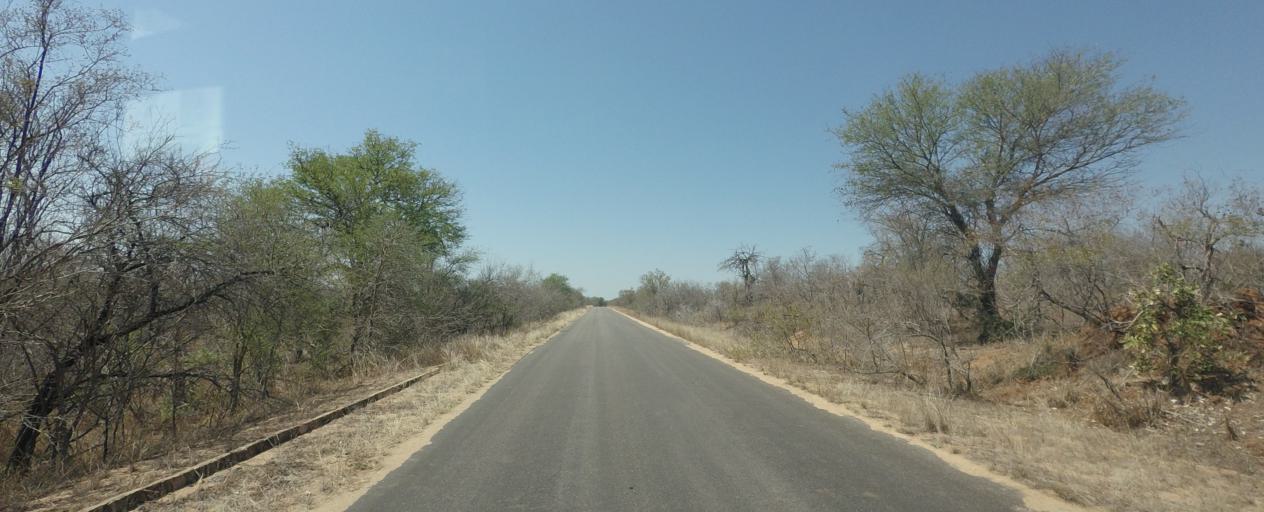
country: ZA
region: Limpopo
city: Thulamahashi
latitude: -24.4141
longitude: 31.5220
